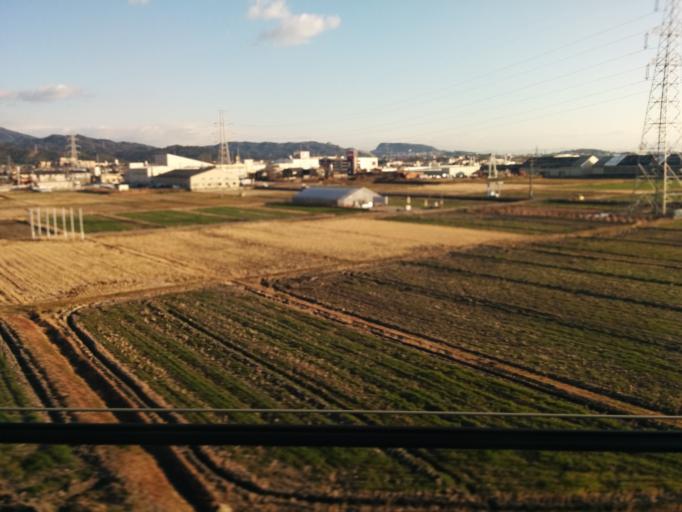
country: JP
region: Gifu
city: Tarui
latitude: 35.3623
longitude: 136.5345
